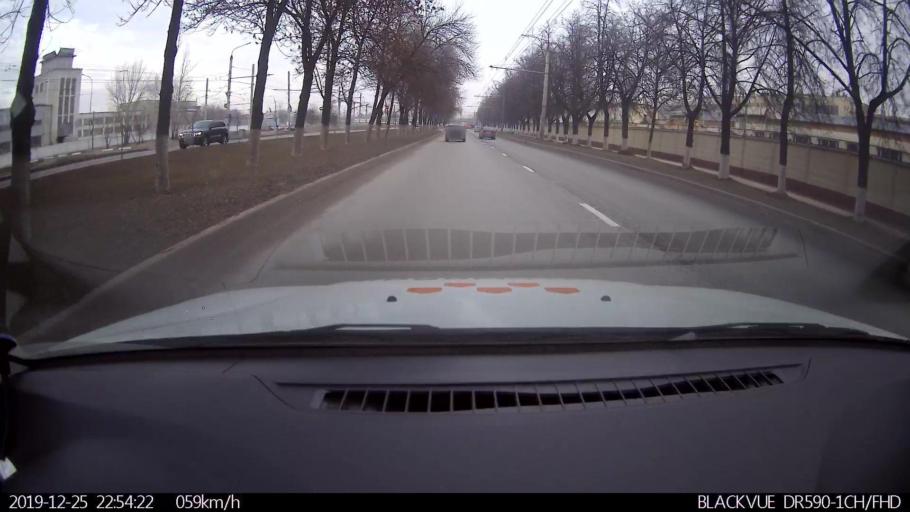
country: RU
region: Nizjnij Novgorod
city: Nizhniy Novgorod
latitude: 56.2554
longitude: 43.8981
